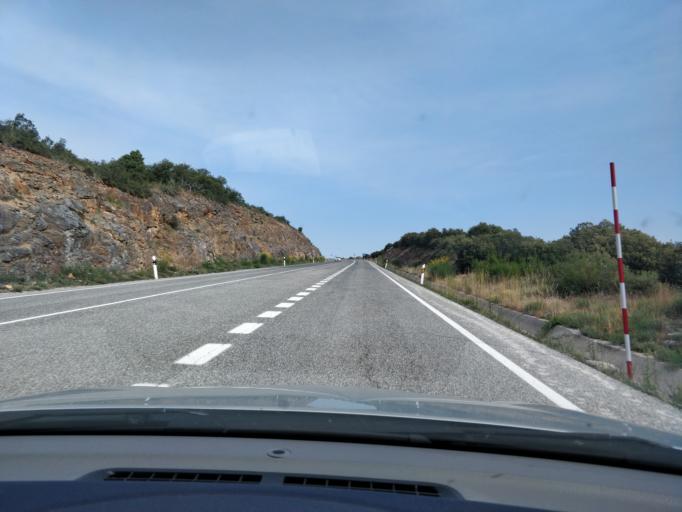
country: ES
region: Castille and Leon
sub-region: Provincia de Burgos
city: Medina de Pomar
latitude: 42.9169
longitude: -3.6137
